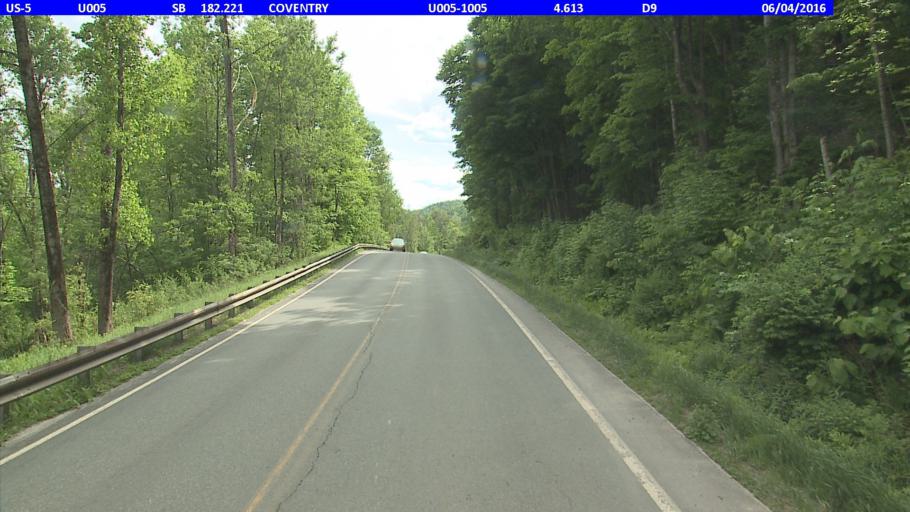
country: US
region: Vermont
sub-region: Orleans County
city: Newport
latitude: 44.9200
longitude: -72.2328
